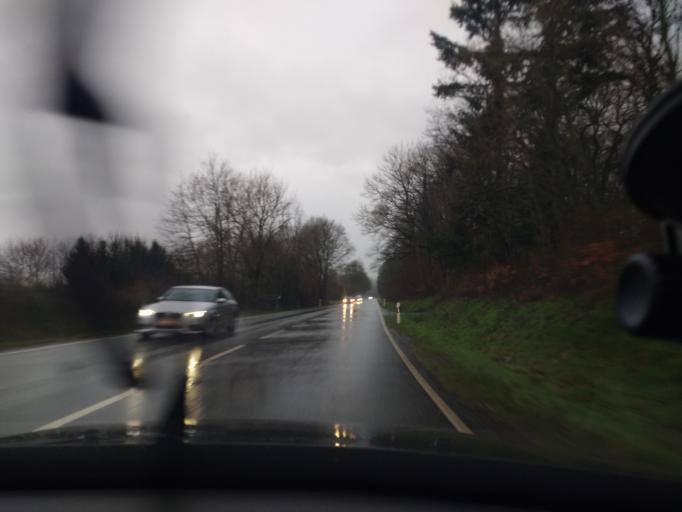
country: DE
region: Rheinland-Pfalz
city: Wiltingen
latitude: 49.7039
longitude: 6.6291
